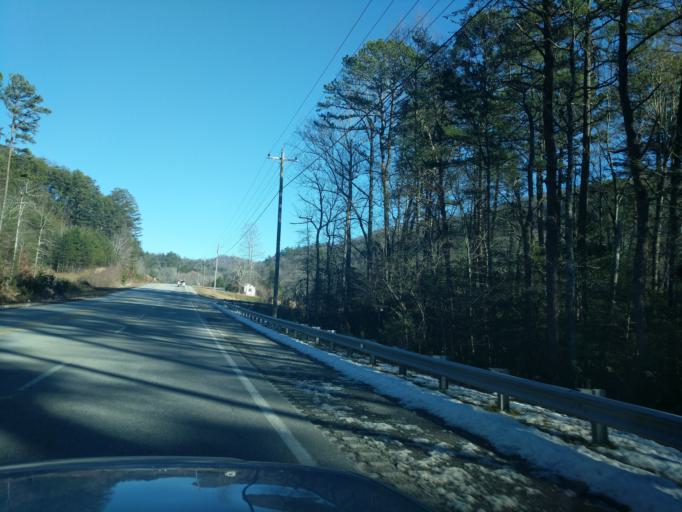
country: US
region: Georgia
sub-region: Rabun County
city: Clayton
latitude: 34.8669
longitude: -83.5360
